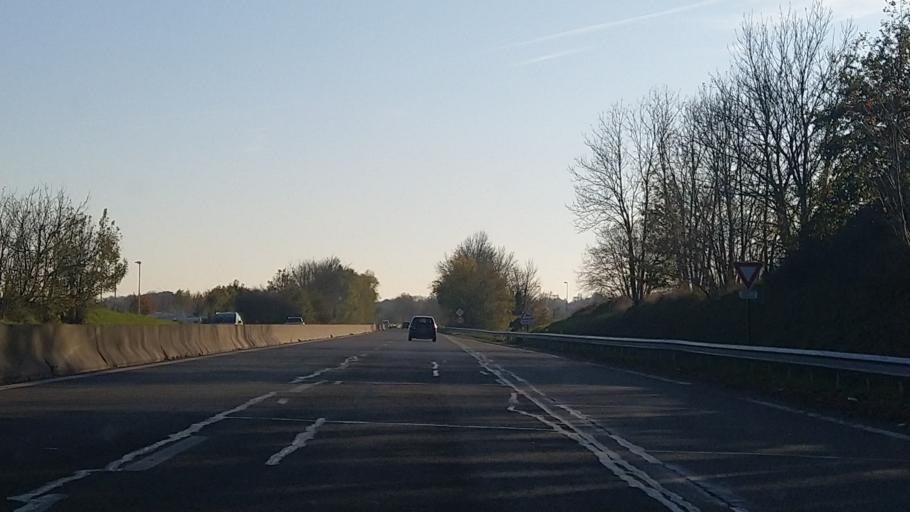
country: FR
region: Ile-de-France
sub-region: Departement du Val-d'Oise
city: Saint-Brice-sous-Foret
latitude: 49.0161
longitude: 2.3519
